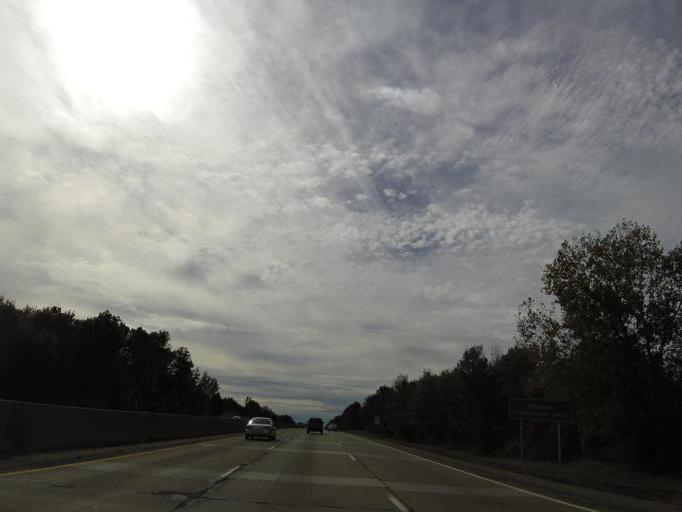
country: US
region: Ohio
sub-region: Summit County
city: Boston Heights
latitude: 41.2270
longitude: -81.4895
